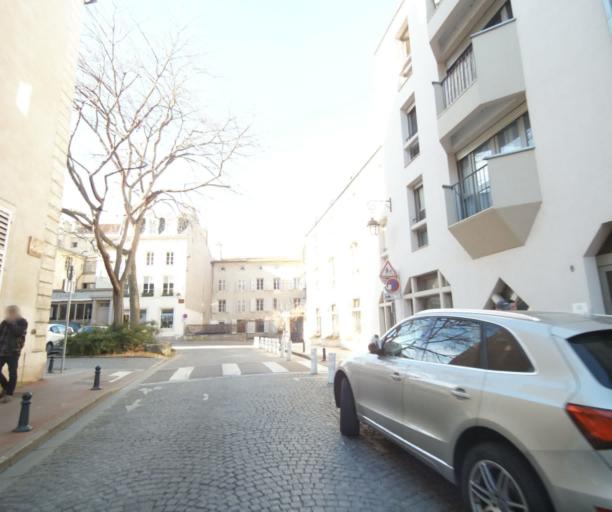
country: FR
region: Lorraine
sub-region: Departement de Meurthe-et-Moselle
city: Nancy
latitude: 48.6967
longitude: 6.1782
